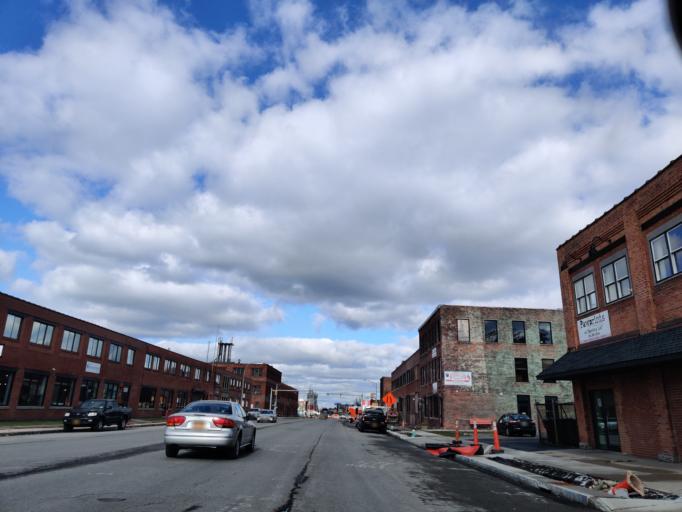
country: US
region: New York
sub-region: Erie County
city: Buffalo
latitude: 42.9175
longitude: -78.8991
